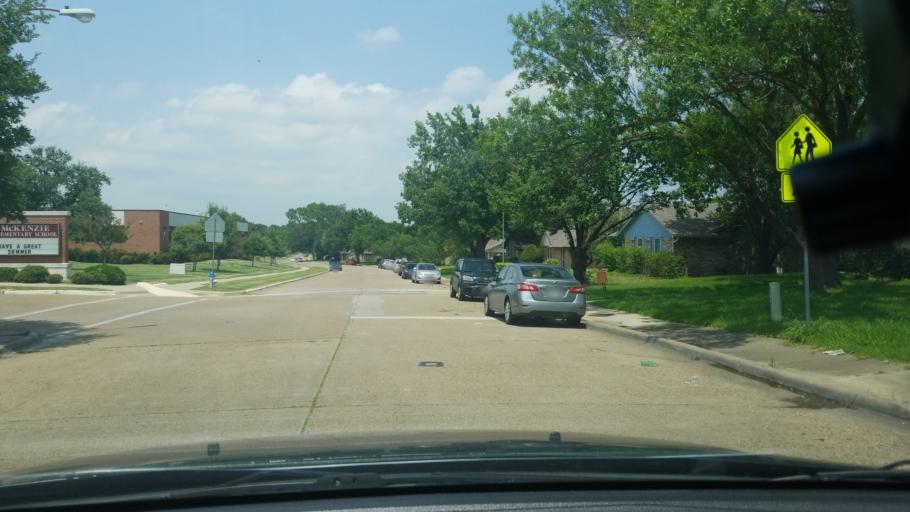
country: US
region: Texas
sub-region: Dallas County
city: Mesquite
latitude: 32.8078
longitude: -96.6437
